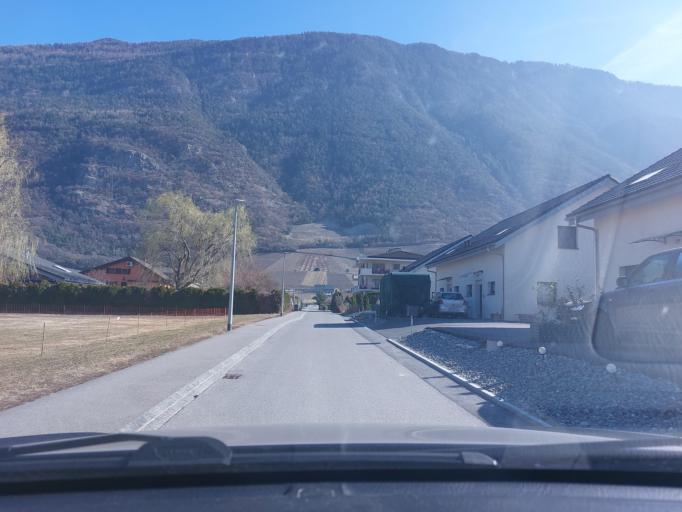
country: CH
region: Valais
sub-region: Martigny District
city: Charrat-les-Chenes
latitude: 46.1256
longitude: 7.1339
